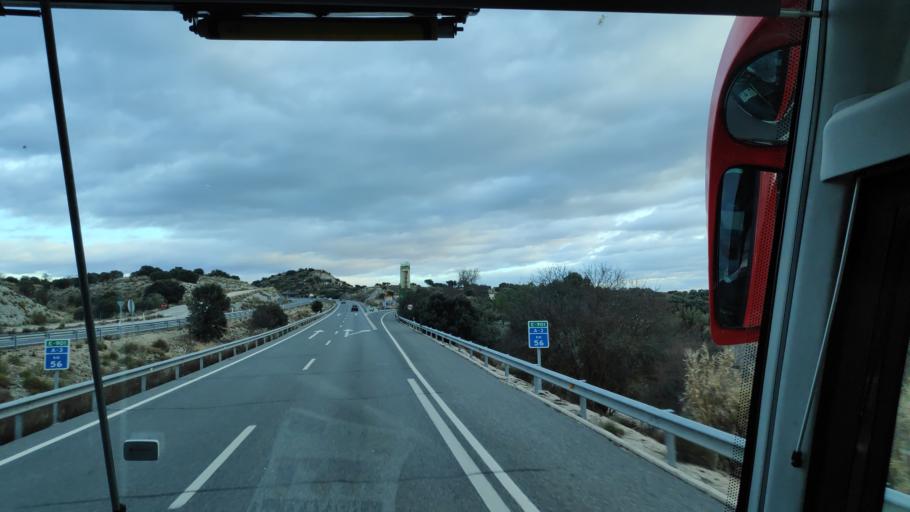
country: ES
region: Madrid
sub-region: Provincia de Madrid
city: Villarejo de Salvanes
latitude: 40.1450
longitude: -3.2152
